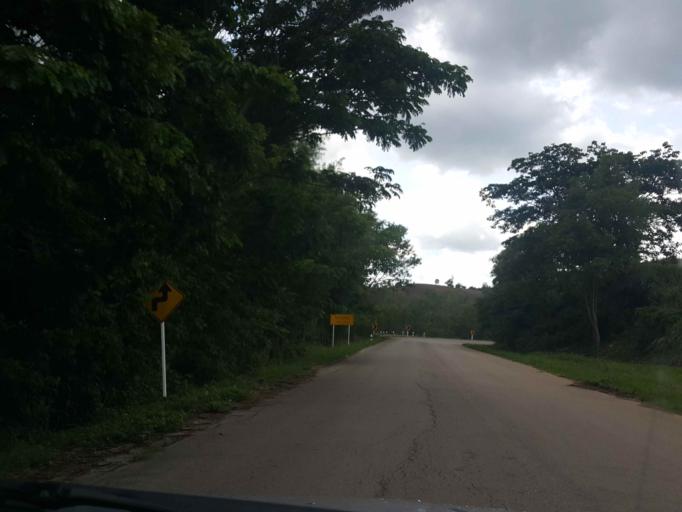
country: TH
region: Phayao
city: Dok Kham Tai
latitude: 18.9650
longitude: 100.0744
